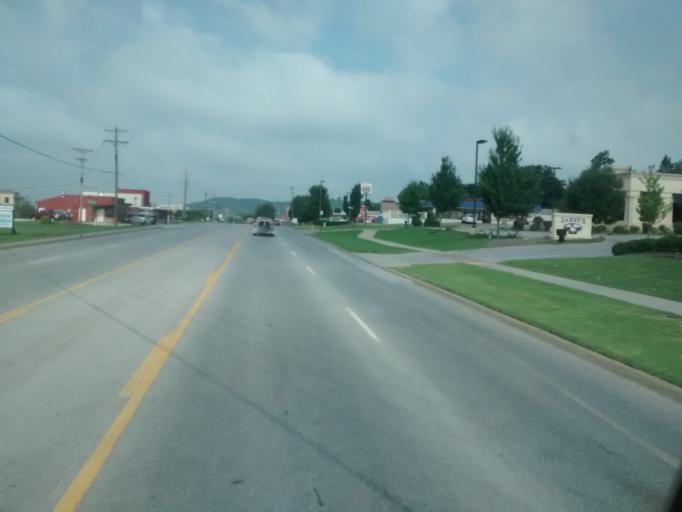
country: US
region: Arkansas
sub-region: Washington County
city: Fayetteville
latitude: 36.0567
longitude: -94.1819
